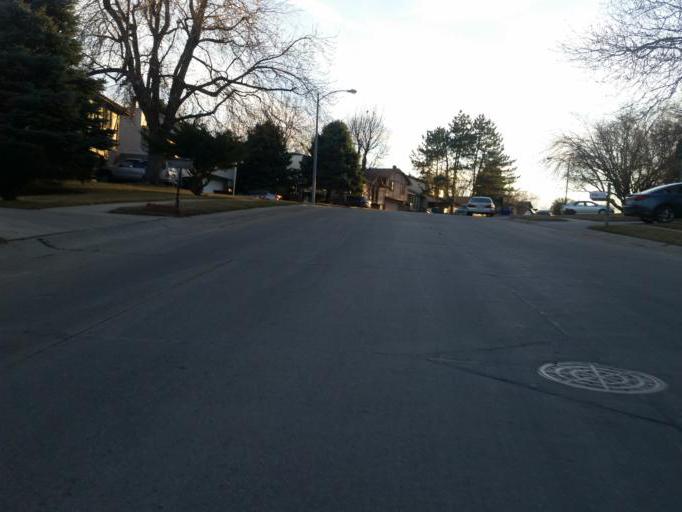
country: US
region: Nebraska
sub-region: Sarpy County
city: Offutt Air Force Base
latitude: 41.1174
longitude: -95.9690
